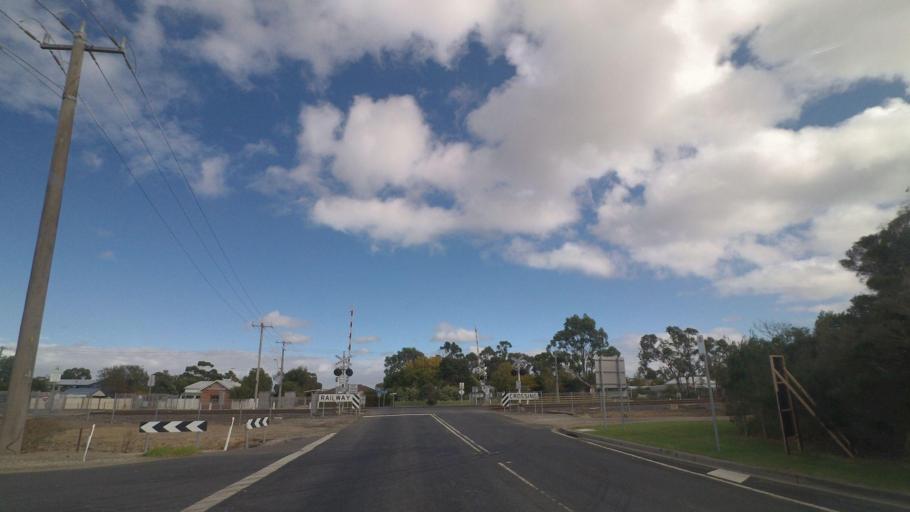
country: AU
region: Victoria
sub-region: Cardinia
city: Garfield
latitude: -38.0844
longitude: 145.6237
